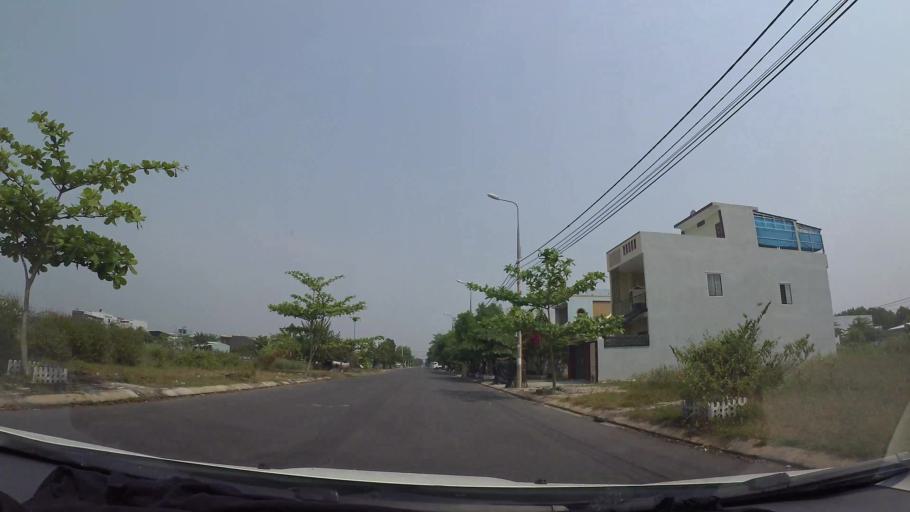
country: VN
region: Da Nang
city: Cam Le
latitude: 15.9803
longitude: 108.2142
